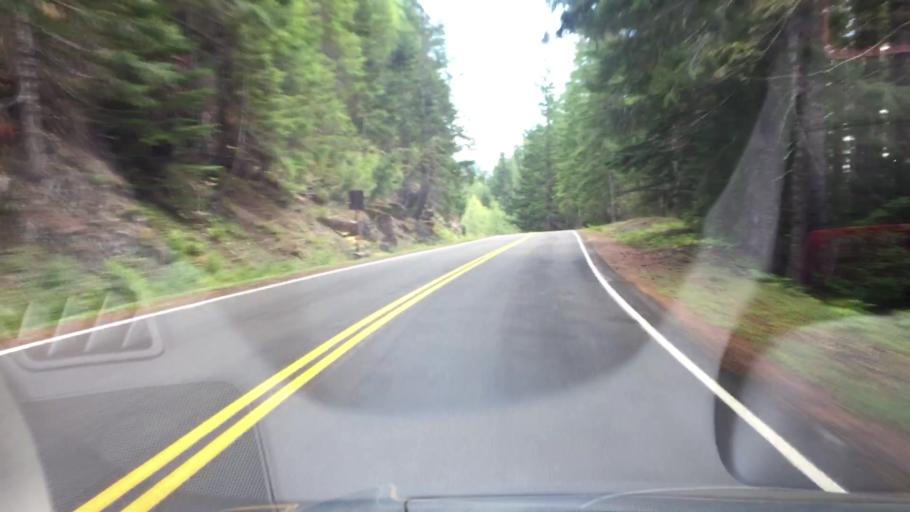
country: US
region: Washington
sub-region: Pierce County
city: Buckley
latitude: 46.7649
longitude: -121.6324
